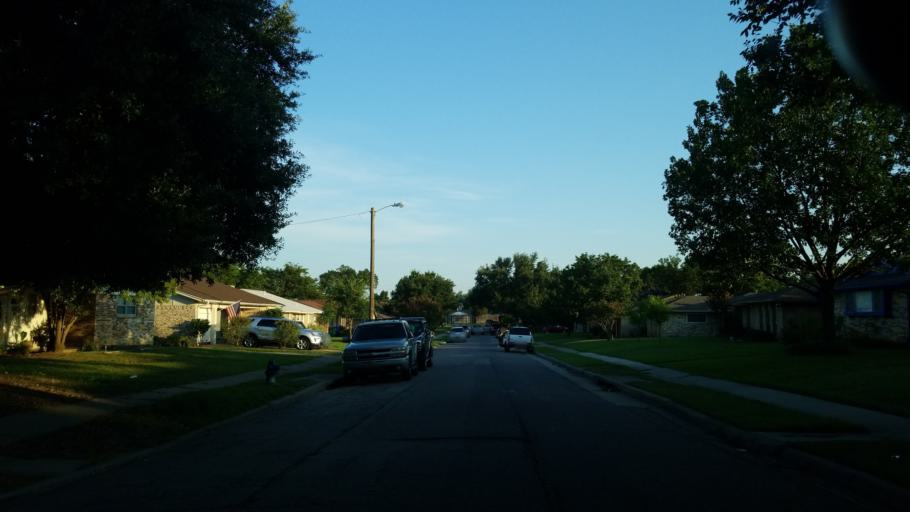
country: US
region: Texas
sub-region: Dallas County
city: Carrollton
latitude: 32.9482
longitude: -96.8870
